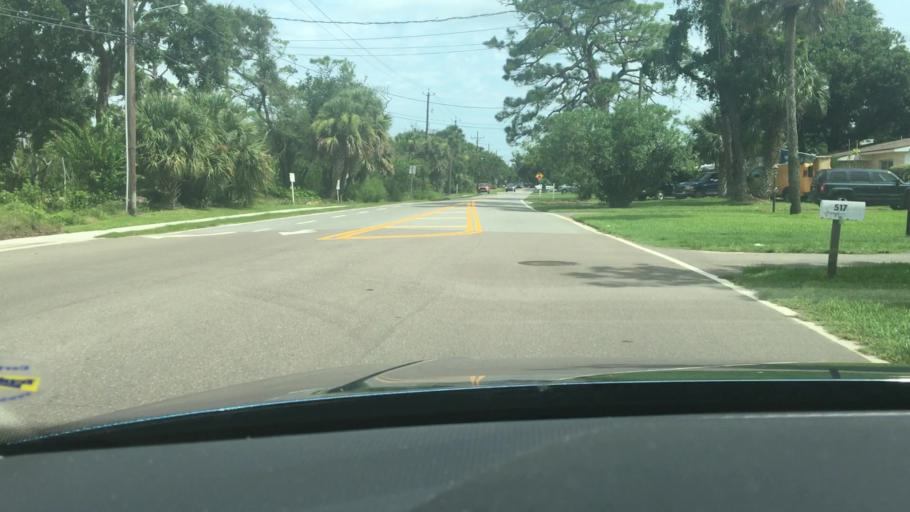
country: US
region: Florida
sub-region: Volusia County
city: New Smyrna Beach
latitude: 29.0327
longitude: -80.9027
